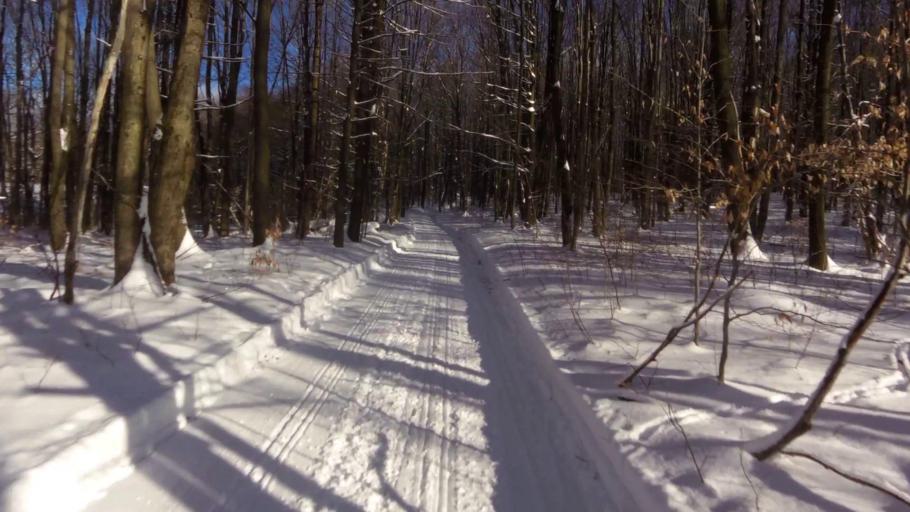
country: US
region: New York
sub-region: Chautauqua County
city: Falconer
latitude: 42.2554
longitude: -79.1434
